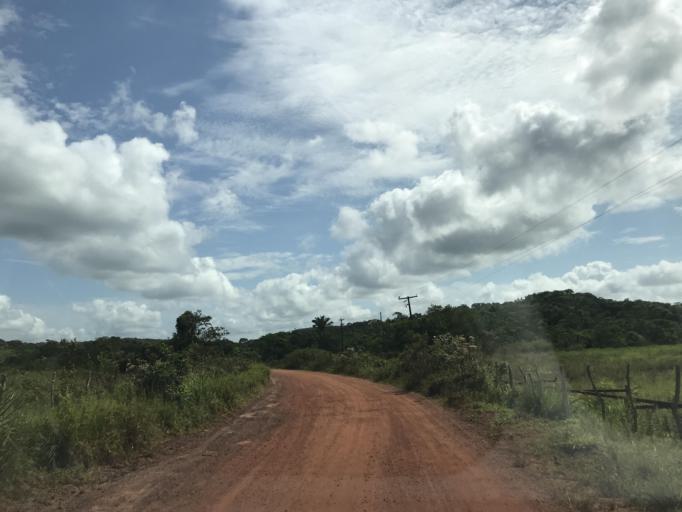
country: BR
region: Bahia
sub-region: Entre Rios
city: Entre Rios
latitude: -12.1645
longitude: -38.0798
